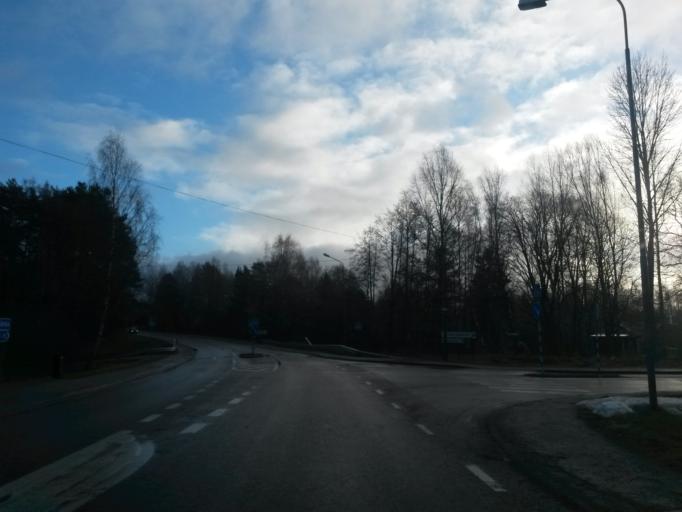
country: SE
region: Vaestra Goetaland
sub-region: Boras Kommun
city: Boras
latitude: 57.8279
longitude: 12.9973
